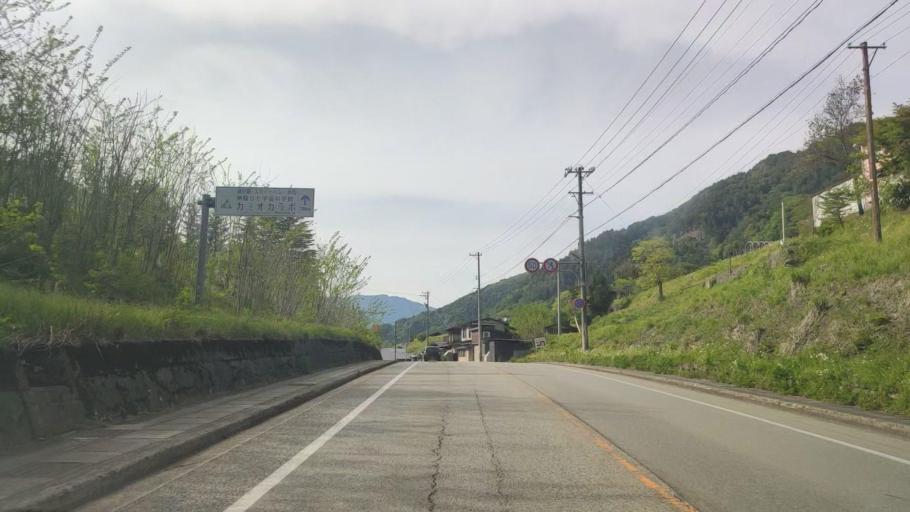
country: JP
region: Gifu
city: Takayama
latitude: 36.3223
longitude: 137.3114
